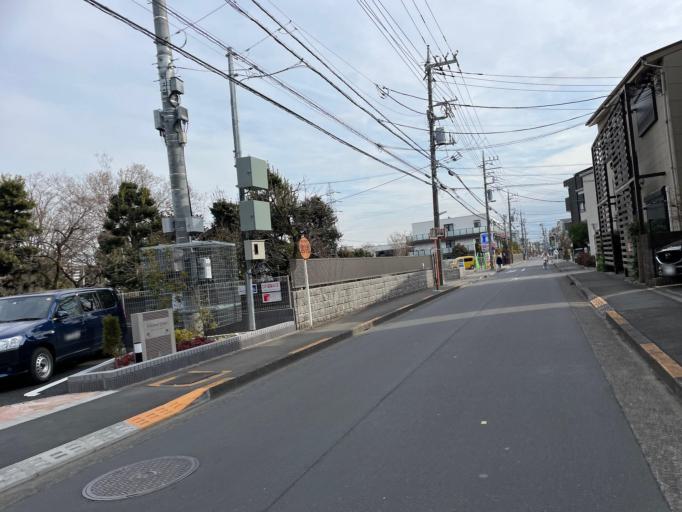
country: JP
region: Tokyo
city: Kamirenjaku
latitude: 35.7001
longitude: 139.5304
